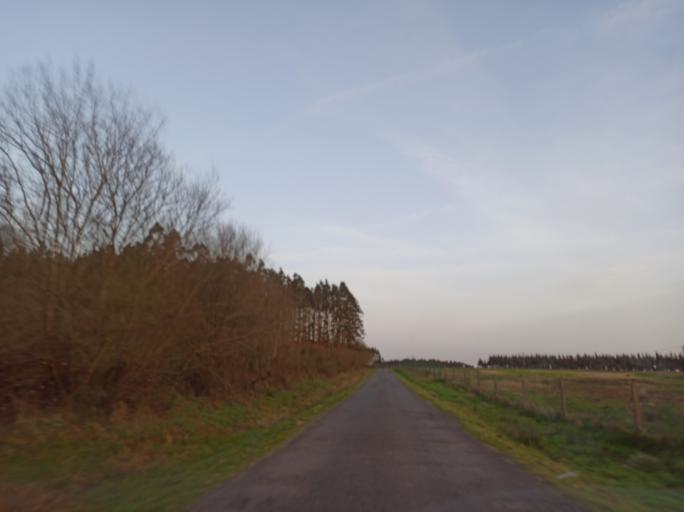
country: ES
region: Galicia
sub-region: Provincia da Coruna
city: Coiros
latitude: 43.1750
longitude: -8.1224
